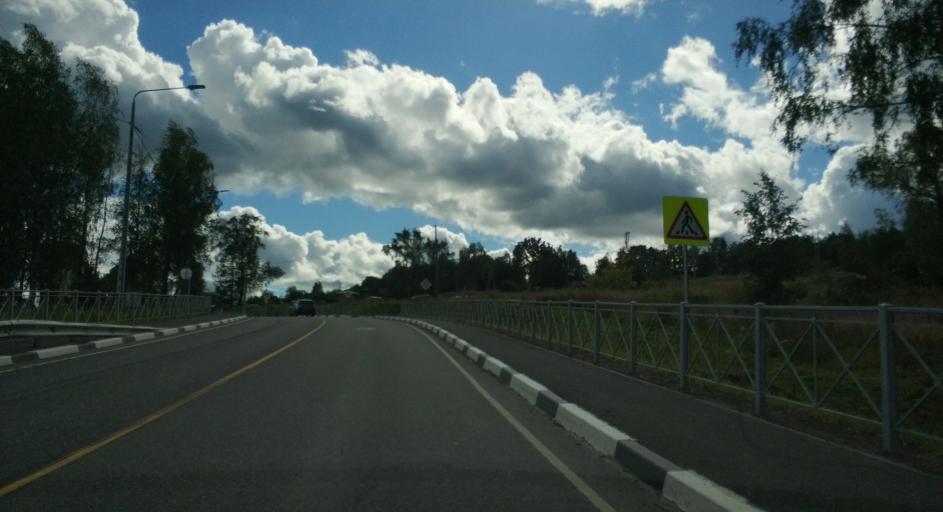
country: RU
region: Republic of Karelia
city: Ruskeala
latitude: 61.9352
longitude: 30.5909
